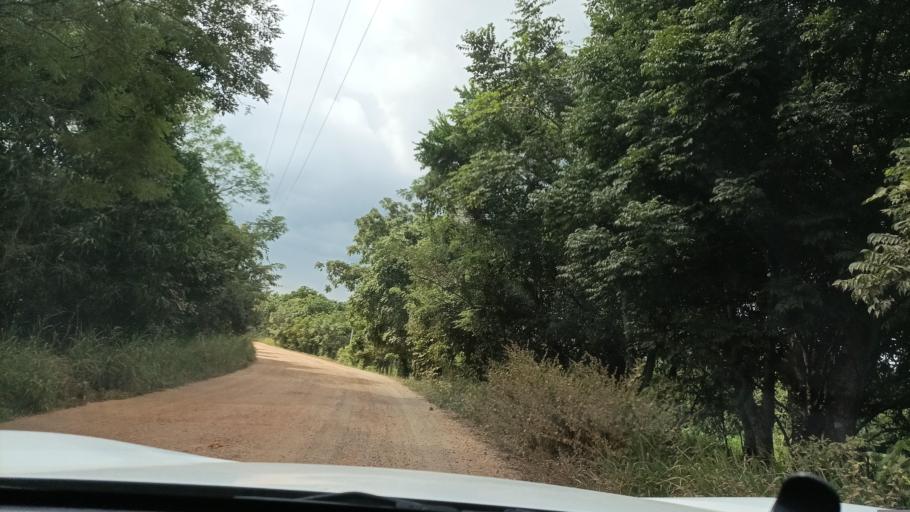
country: MX
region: Veracruz
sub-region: Chinameca
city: Chacalapa
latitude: 18.0827
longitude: -94.6842
